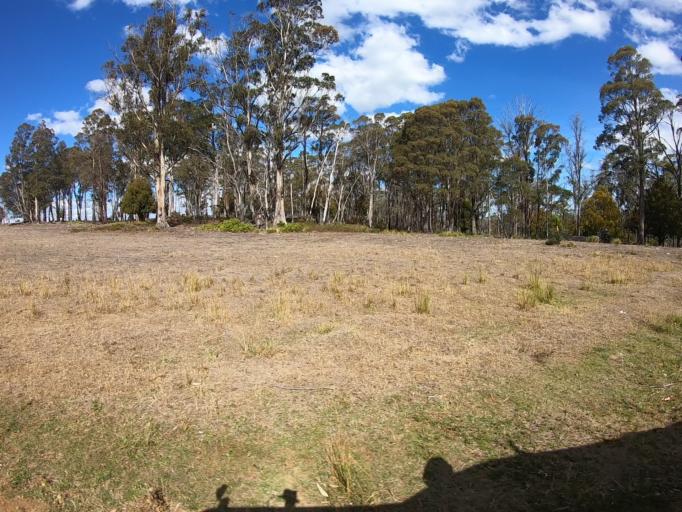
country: AU
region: Tasmania
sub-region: Brighton
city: Bridgewater
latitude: -42.4971
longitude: 147.4220
